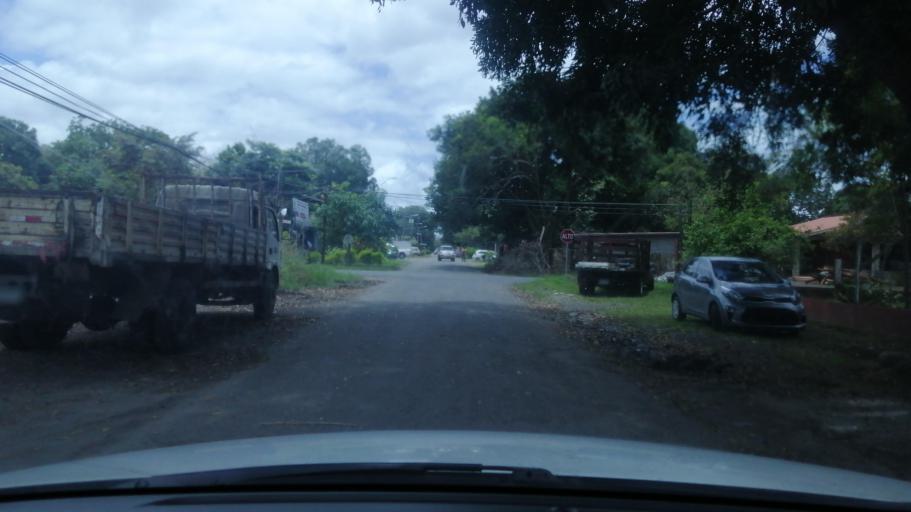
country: PA
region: Chiriqui
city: David
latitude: 8.4412
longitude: -82.4291
